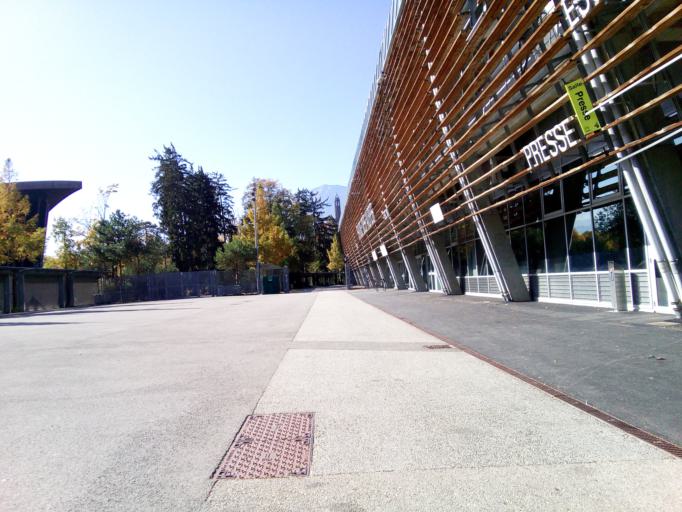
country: FR
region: Rhone-Alpes
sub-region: Departement de l'Isere
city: La Tronche
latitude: 45.1872
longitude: 5.7412
